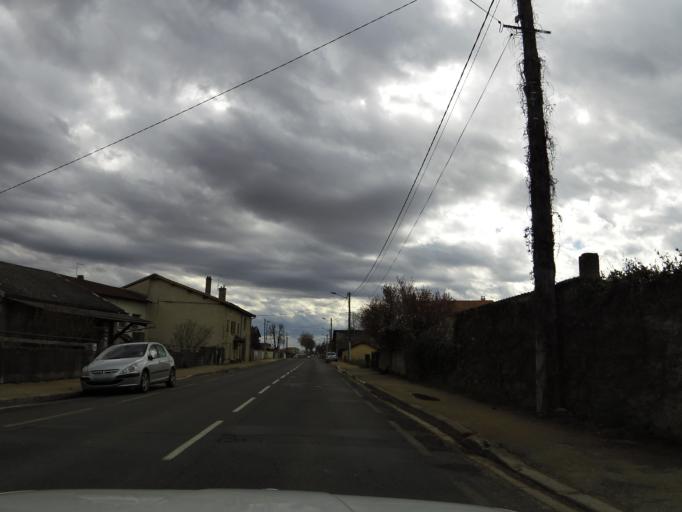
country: FR
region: Rhone-Alpes
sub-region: Departement de l'Ain
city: Meximieux
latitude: 45.9188
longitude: 5.2217
